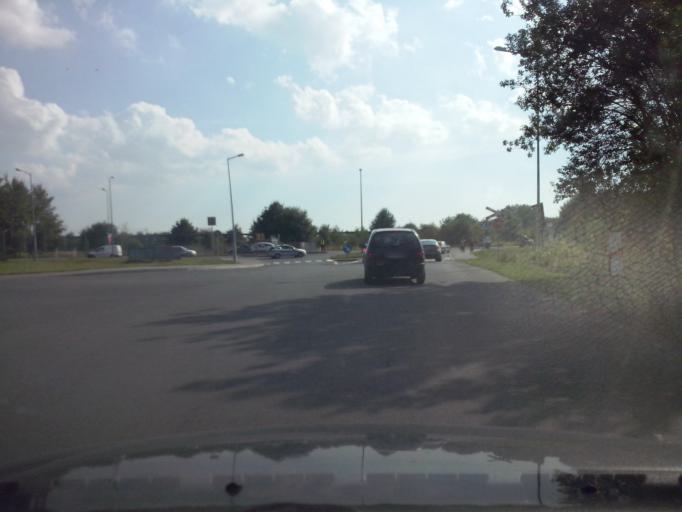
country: PL
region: Subcarpathian Voivodeship
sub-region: Powiat mielecki
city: Mielec
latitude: 50.3075
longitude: 21.4535
